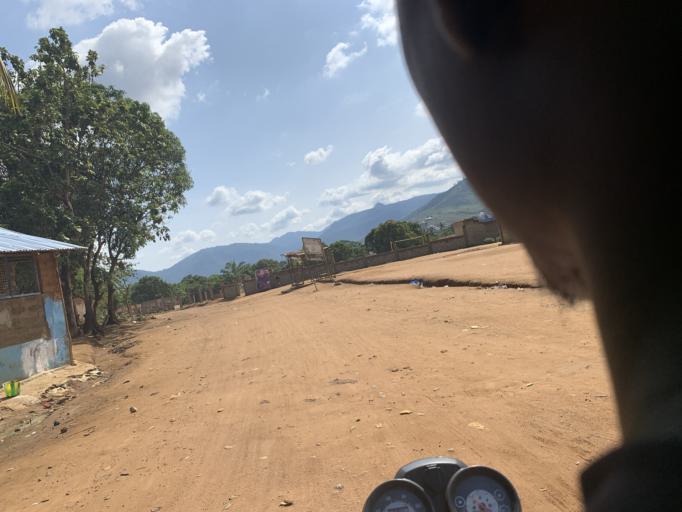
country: SL
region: Western Area
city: Waterloo
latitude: 8.3321
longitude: -13.0580
